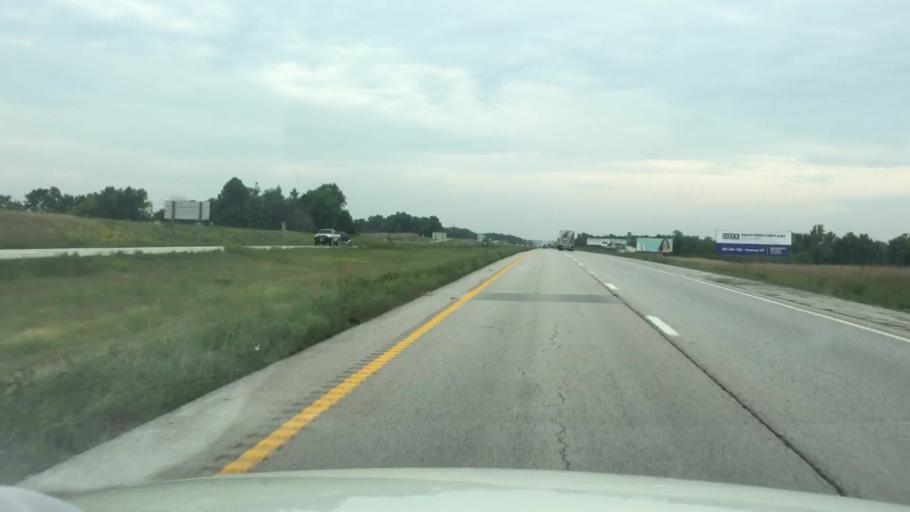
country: US
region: Missouri
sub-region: Clinton County
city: Cameron
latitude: 39.7197
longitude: -94.2229
